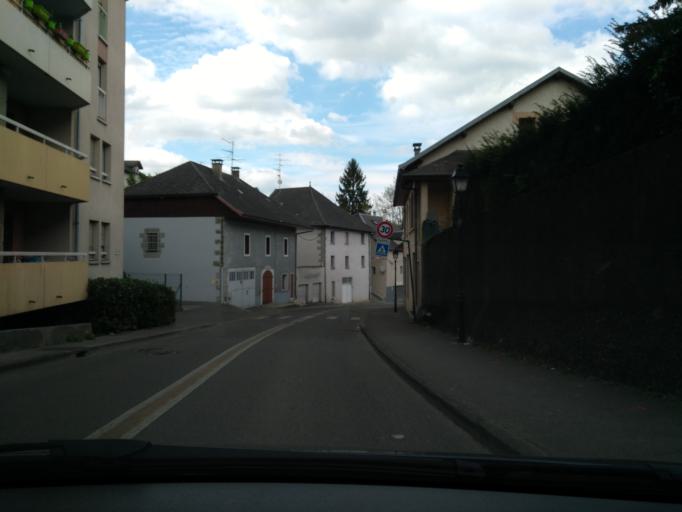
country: FR
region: Rhone-Alpes
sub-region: Departement de la Haute-Savoie
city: Rumilly
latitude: 45.8653
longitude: 5.9407
